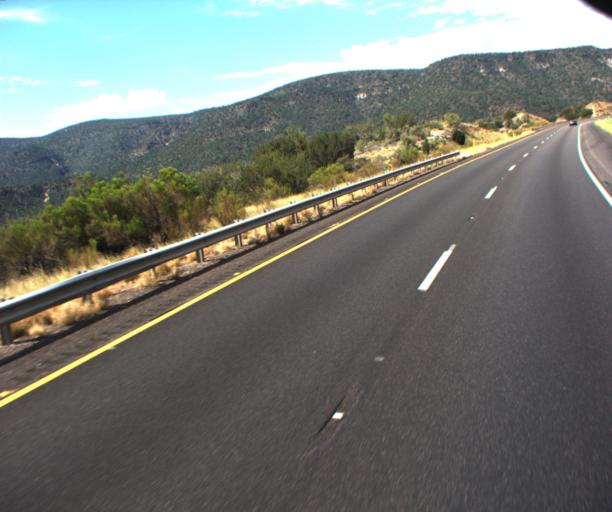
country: US
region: Arizona
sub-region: Yavapai County
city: Camp Verde
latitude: 34.5410
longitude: -111.9099
